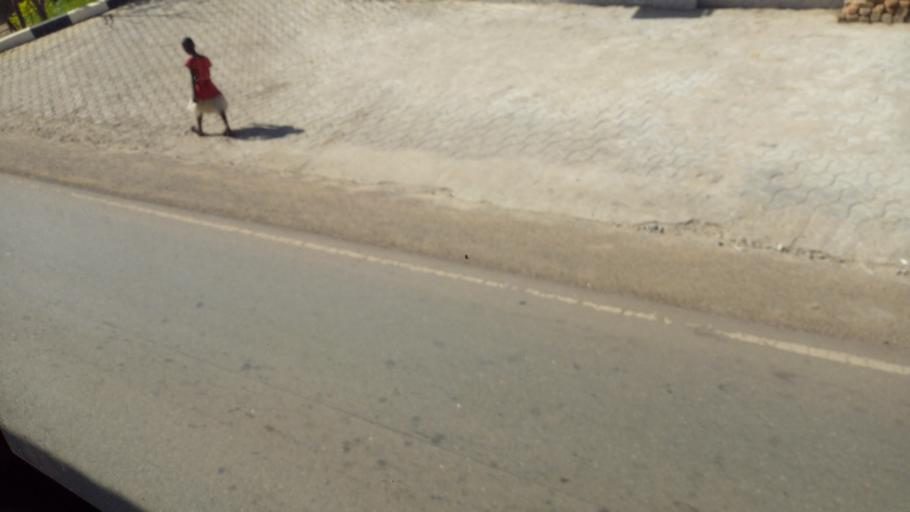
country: UG
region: Central Region
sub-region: Lyantonde District
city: Lyantonde
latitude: -0.4042
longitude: 31.1570
